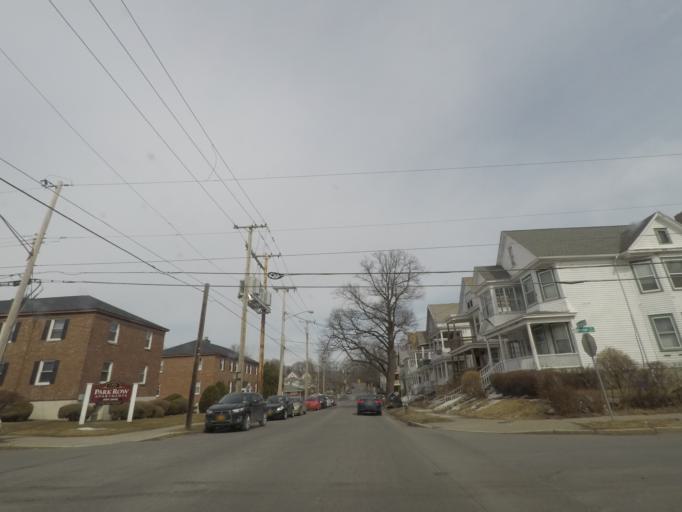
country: US
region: New York
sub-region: Albany County
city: Albany
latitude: 42.6557
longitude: -73.7838
